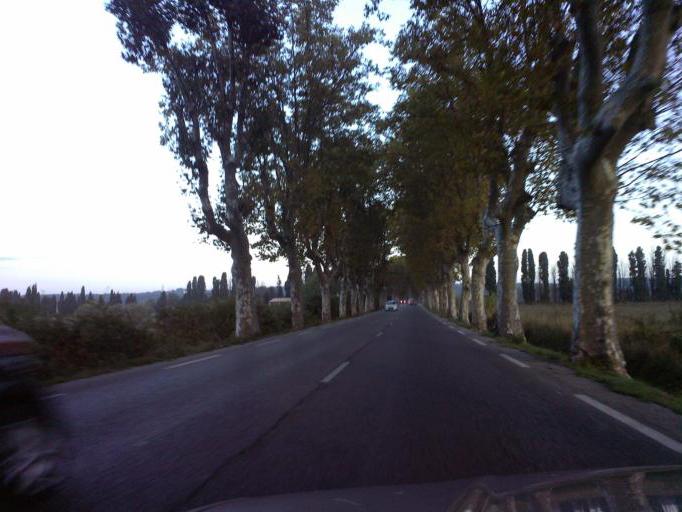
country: FR
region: Provence-Alpes-Cote d'Azur
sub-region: Departement des Bouches-du-Rhone
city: Saint-Cannat
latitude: 43.6315
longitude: 5.2857
